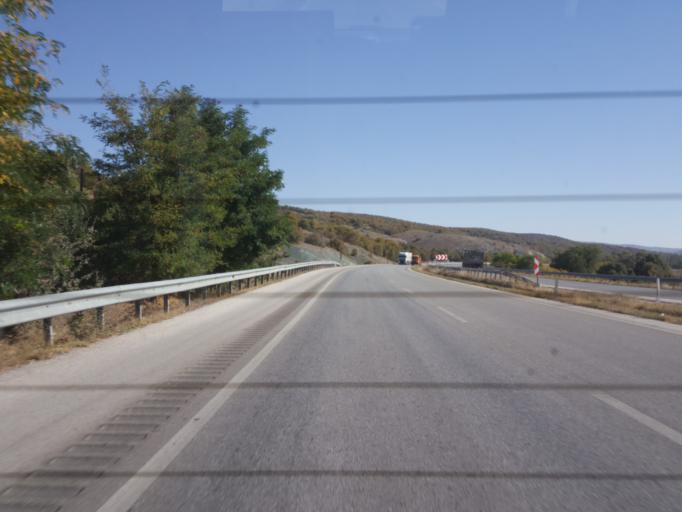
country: TR
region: Corum
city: Alaca
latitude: 40.3107
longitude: 34.6593
